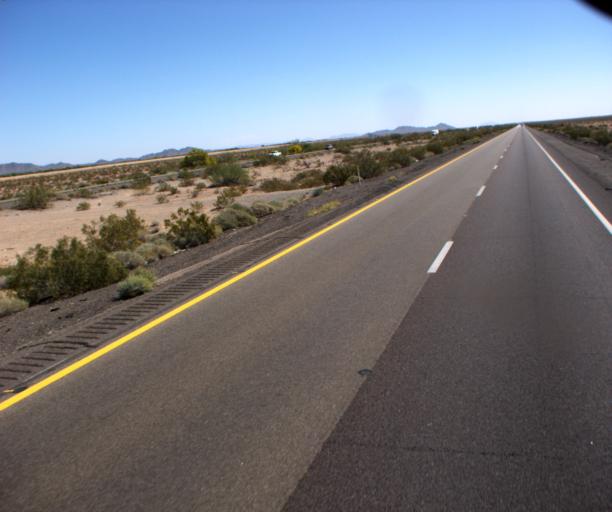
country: US
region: Arizona
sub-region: La Paz County
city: Salome
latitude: 33.6062
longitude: -113.6022
